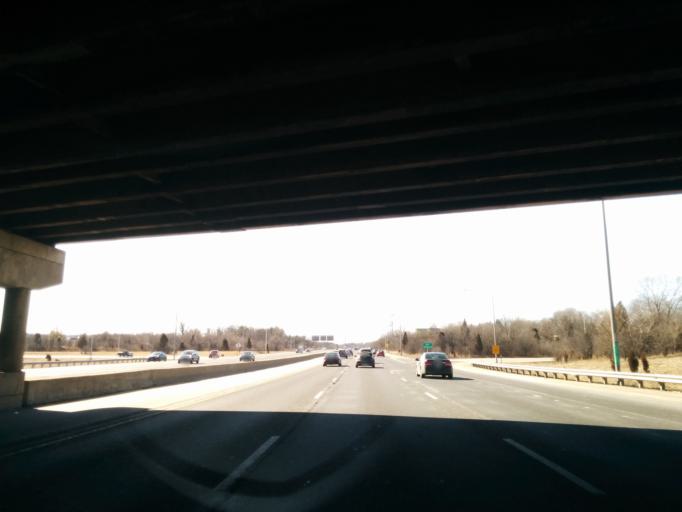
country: US
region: Illinois
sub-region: DuPage County
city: Darien
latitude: 41.7315
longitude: -87.9731
